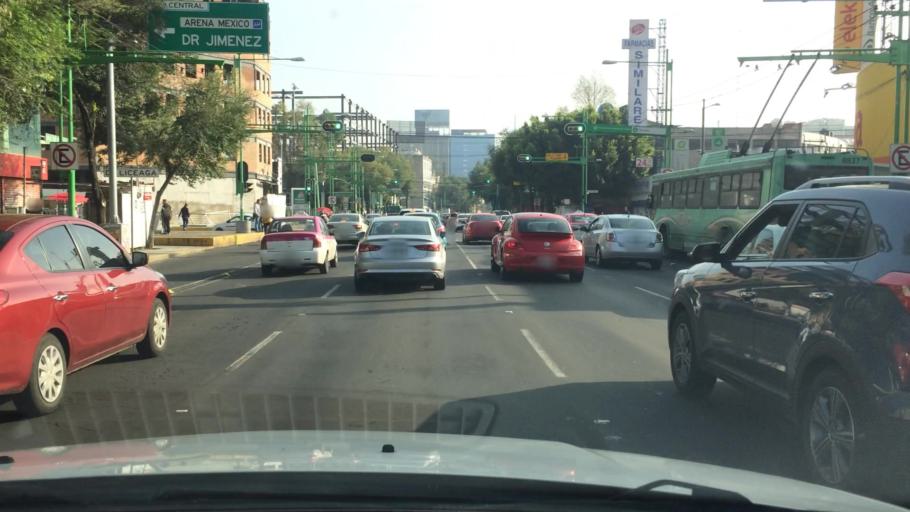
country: MX
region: Mexico City
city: Mexico City
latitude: 19.4211
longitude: -99.1433
